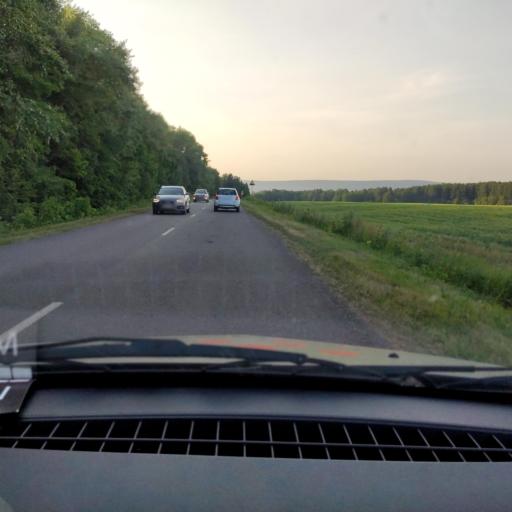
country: RU
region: Bashkortostan
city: Avdon
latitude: 54.5665
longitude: 55.6781
